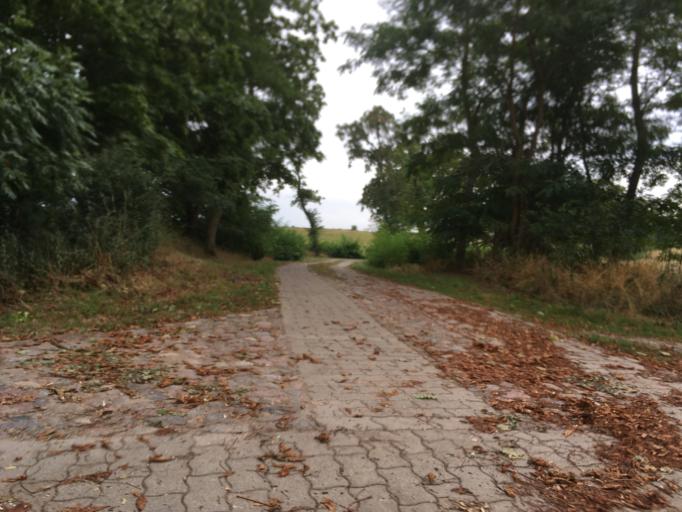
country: DE
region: Brandenburg
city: Passow
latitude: 53.1114
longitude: 14.1234
